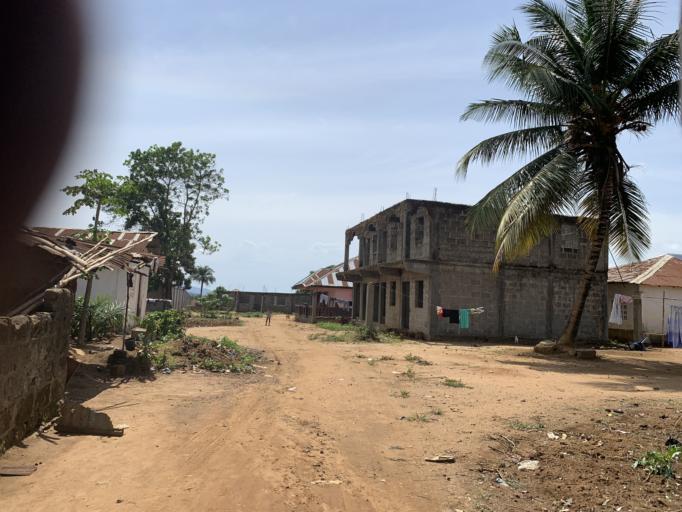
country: SL
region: Western Area
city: Waterloo
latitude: 8.3409
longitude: -13.0496
